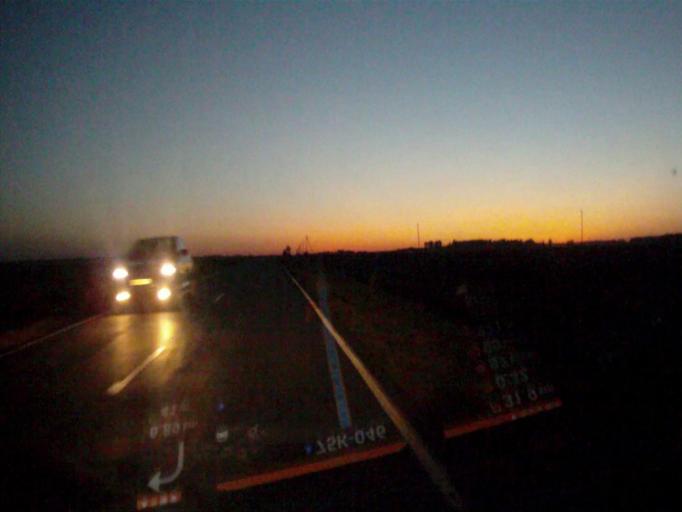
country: RU
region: Chelyabinsk
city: Chebarkul'
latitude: 55.2204
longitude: 60.5568
